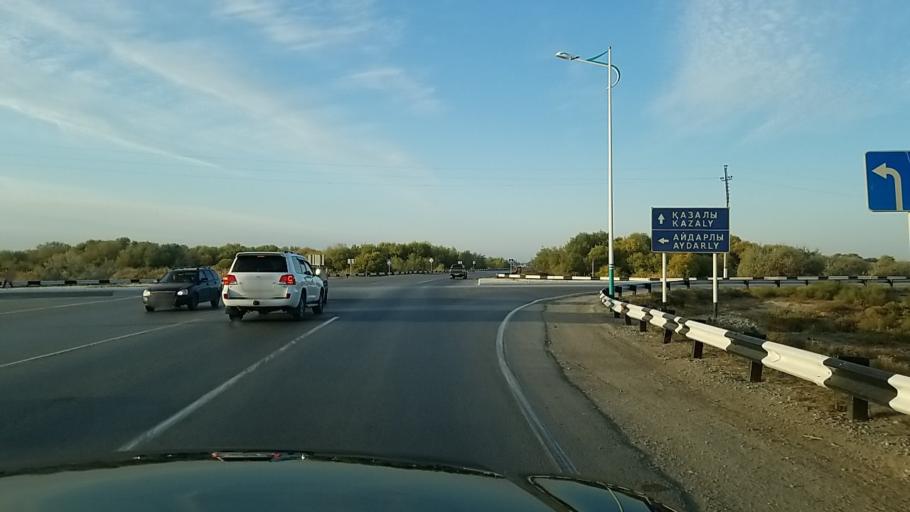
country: KZ
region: Qyzylorda
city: Tasboget
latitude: 44.7744
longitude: 65.5017
